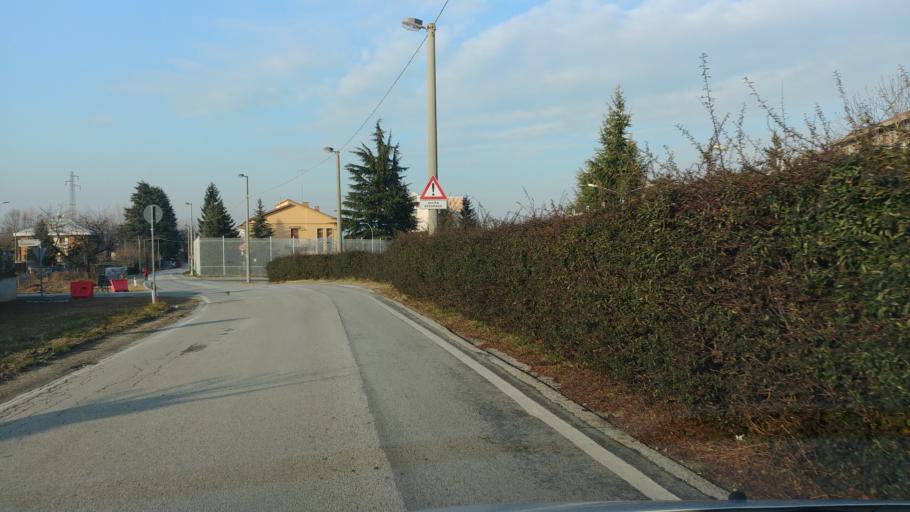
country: IT
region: Piedmont
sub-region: Provincia di Cuneo
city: Cuneo
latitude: 44.4021
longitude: 7.5367
